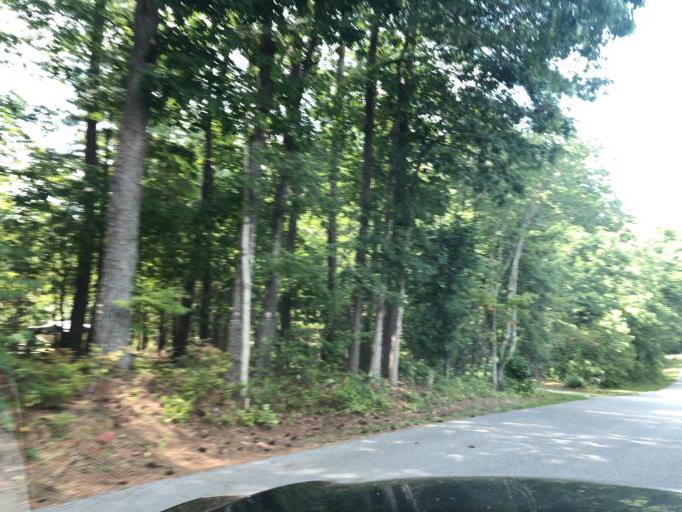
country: US
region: Tennessee
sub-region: Franklin County
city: Sewanee
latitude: 35.1958
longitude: -85.9255
